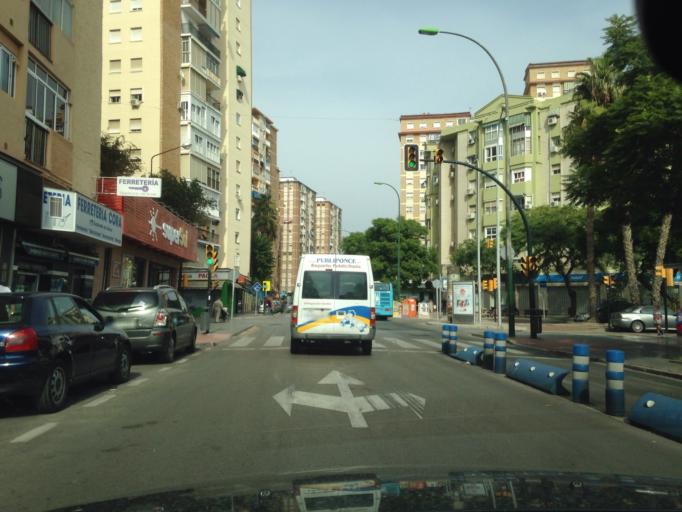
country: ES
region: Andalusia
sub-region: Provincia de Malaga
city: Malaga
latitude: 36.7047
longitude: -4.4369
